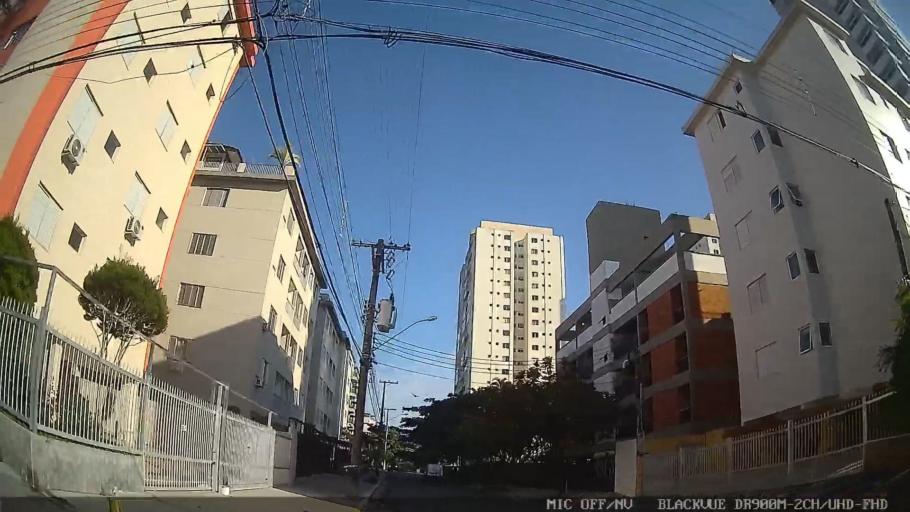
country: BR
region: Sao Paulo
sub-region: Guaruja
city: Guaruja
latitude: -24.0104
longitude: -46.2740
